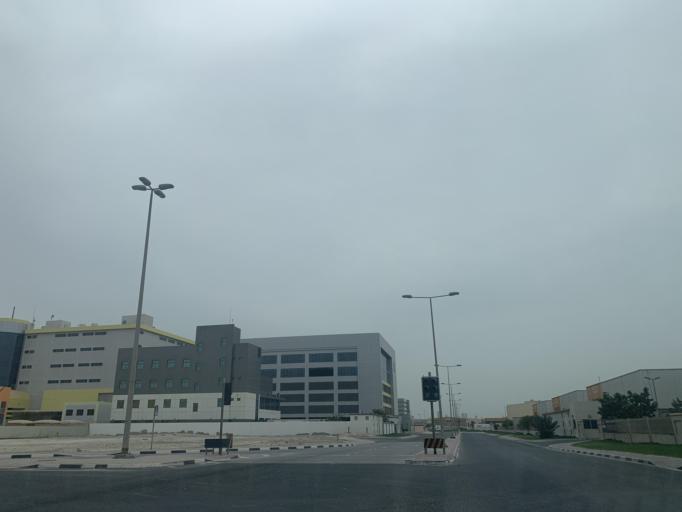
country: BH
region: Muharraq
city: Al Hadd
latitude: 26.2149
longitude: 50.6730
